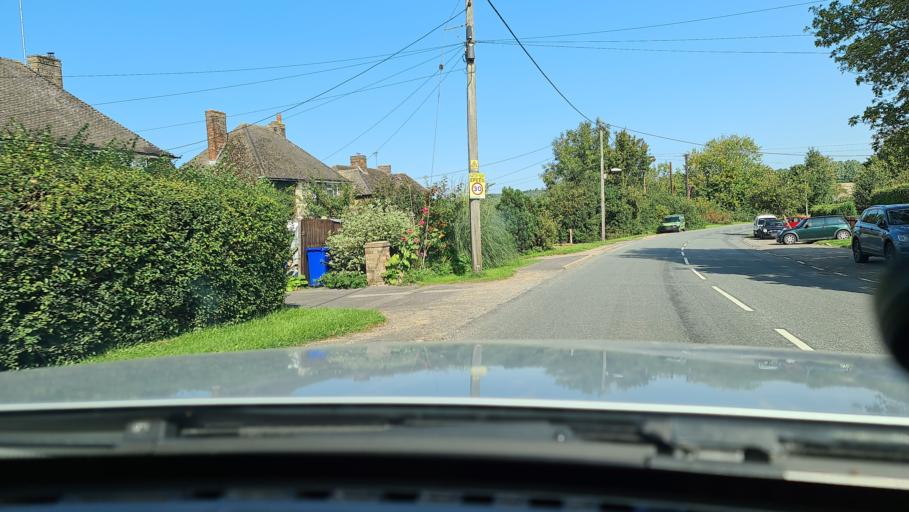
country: GB
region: England
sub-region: Northamptonshire
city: Brackley
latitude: 52.1401
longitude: -1.1597
